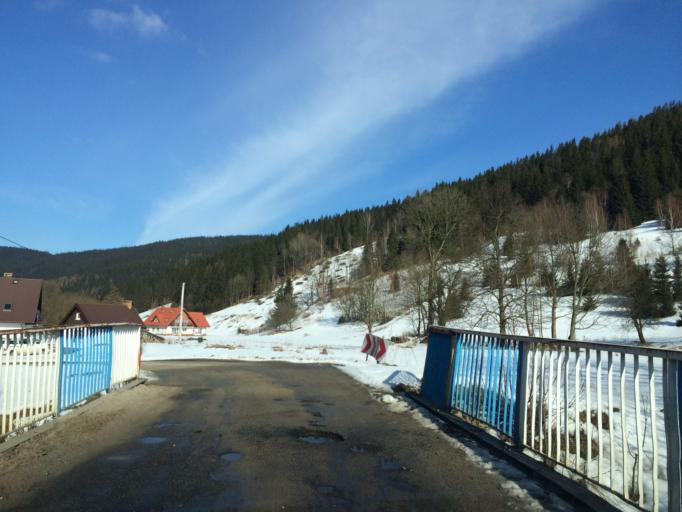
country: CZ
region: Olomoucky
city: Vapenna
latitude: 50.2675
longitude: 17.0030
